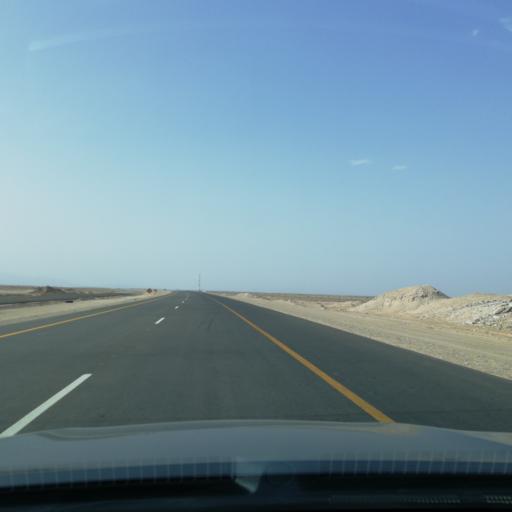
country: OM
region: Muhafazat ad Dakhiliyah
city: Adam
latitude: 22.1296
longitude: 57.5257
